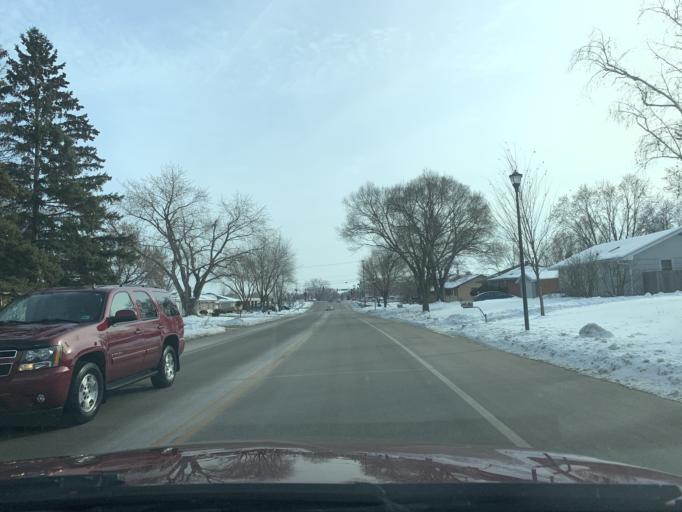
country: US
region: Minnesota
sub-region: Washington County
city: Saint Paul Park
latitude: 44.8333
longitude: -92.9689
